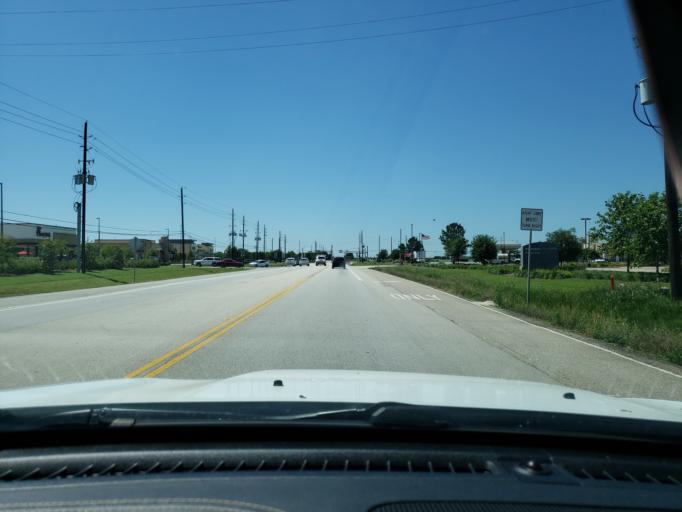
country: US
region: Texas
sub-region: Fort Bend County
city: Fulshear
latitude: 29.6977
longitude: -95.8460
